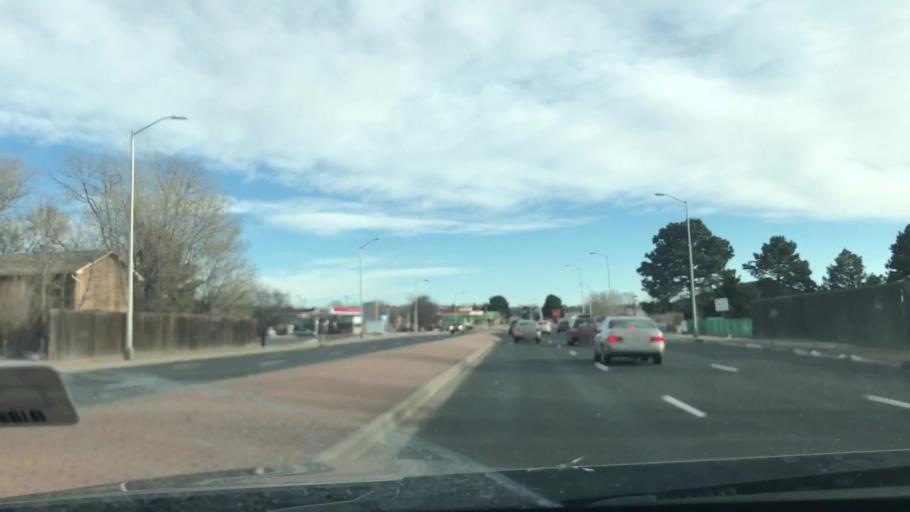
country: US
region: Colorado
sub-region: El Paso County
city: Cimarron Hills
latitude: 38.8959
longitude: -104.7599
